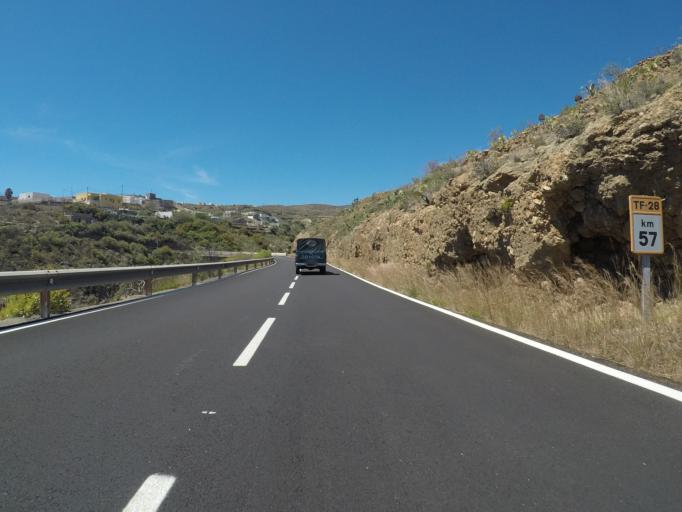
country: ES
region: Canary Islands
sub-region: Provincia de Santa Cruz de Tenerife
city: Lomo de Arico
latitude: 28.1741
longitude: -16.4910
